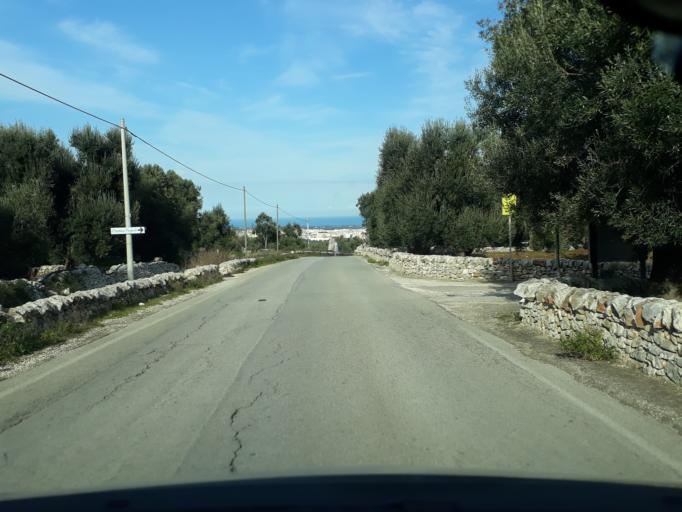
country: IT
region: Apulia
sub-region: Provincia di Brindisi
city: Lamie di Olimpie-Selva
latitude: 40.8108
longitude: 17.3553
